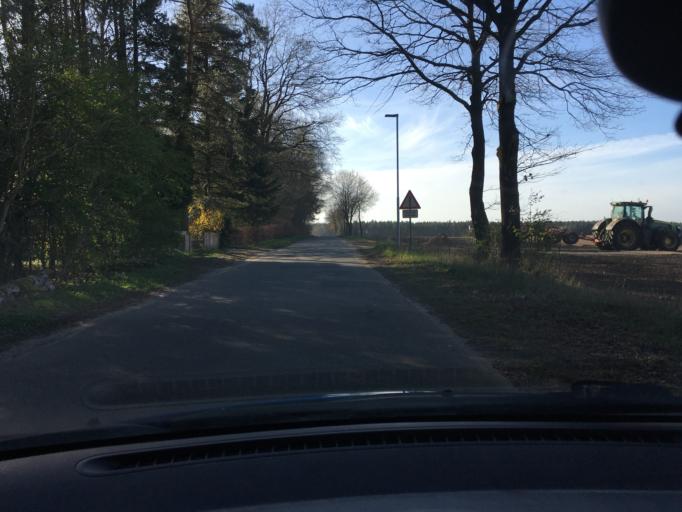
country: DE
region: Lower Saxony
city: Bispingen
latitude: 53.1092
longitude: 10.0242
